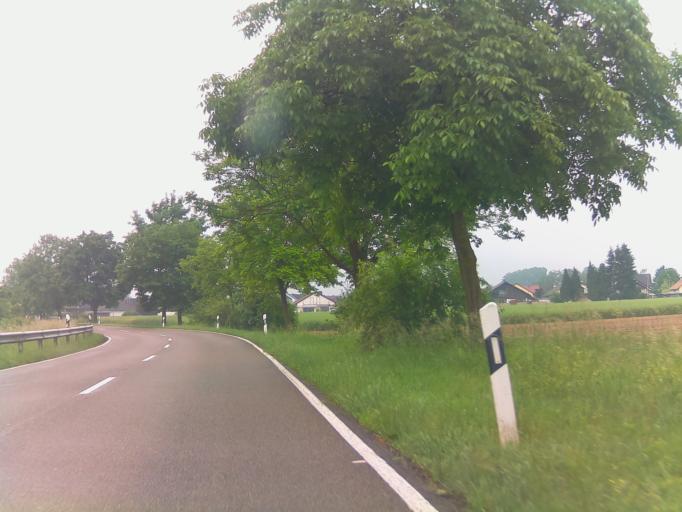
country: DE
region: Rheinland-Pfalz
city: Kuhardt
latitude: 49.1519
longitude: 8.3154
